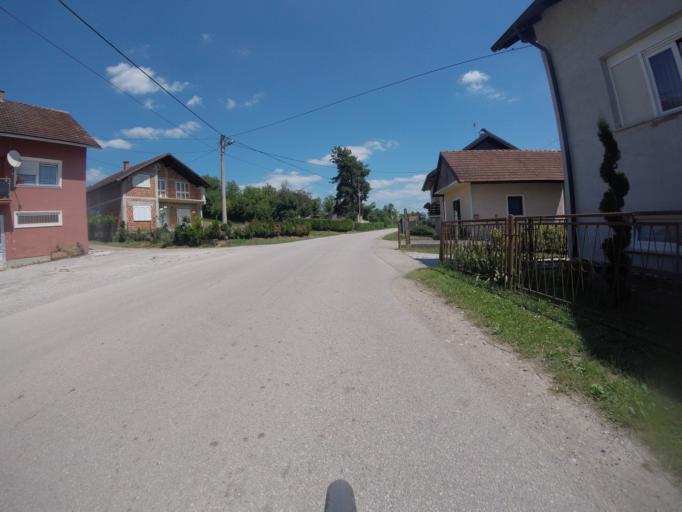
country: HR
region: Karlovacka
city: Ozalj
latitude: 45.6569
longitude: 15.5106
